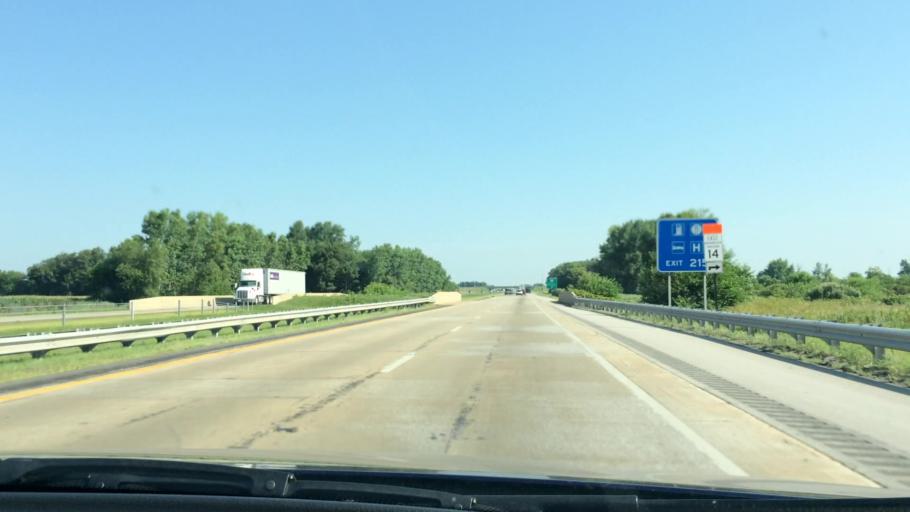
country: US
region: Indiana
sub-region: Jasper County
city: Rensselaer
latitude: 40.9313
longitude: -87.2190
